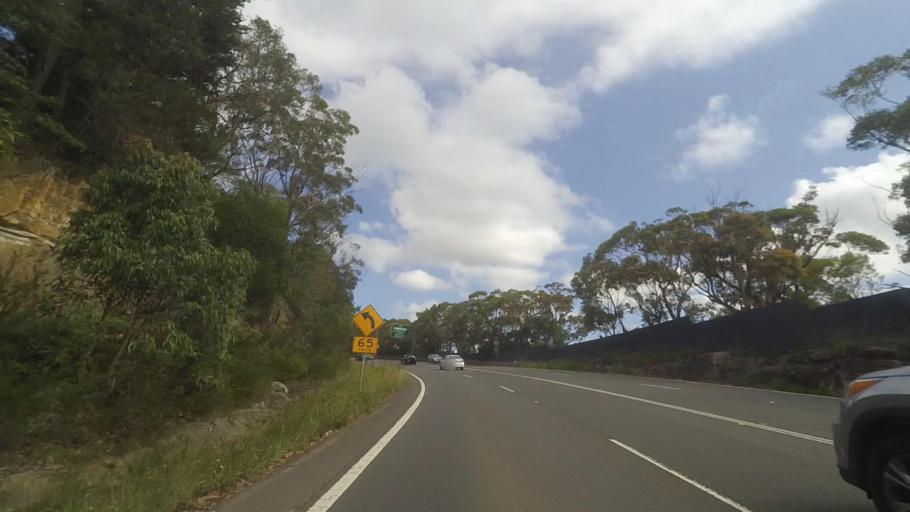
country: AU
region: New South Wales
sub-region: Sutherland Shire
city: Heathcote
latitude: -34.0782
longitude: 151.0081
